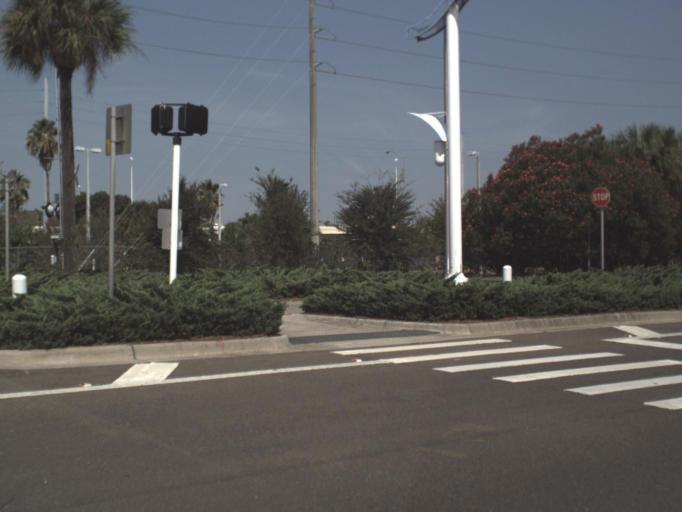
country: US
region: Florida
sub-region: Hillsborough County
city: Tampa
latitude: 27.9506
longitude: -82.4490
